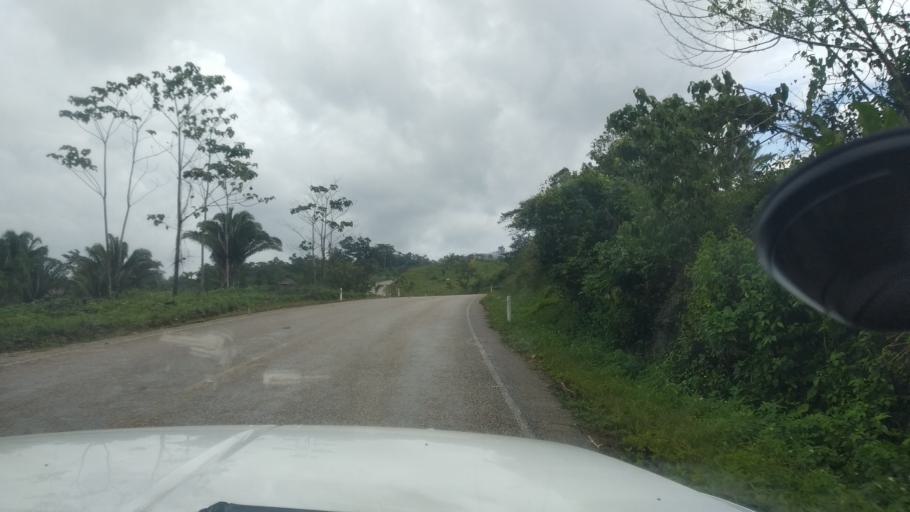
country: GT
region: Peten
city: San Luis
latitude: 16.1989
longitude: -89.1559
